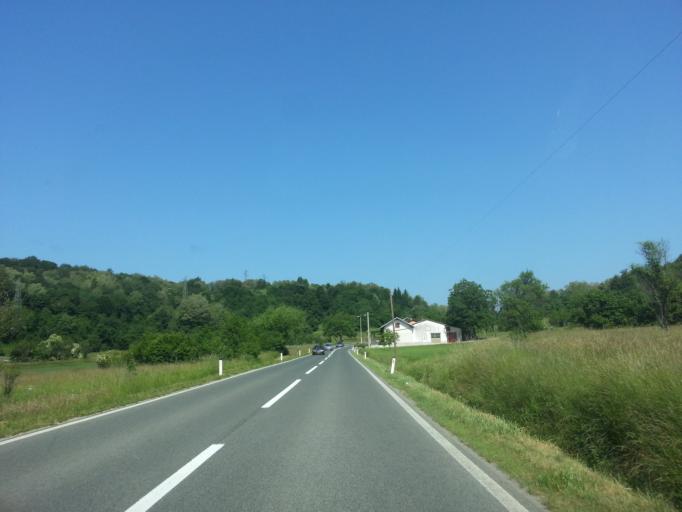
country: SI
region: Ilirska Bistrica
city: Ilirska Bistrica
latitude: 45.5081
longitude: 14.2613
